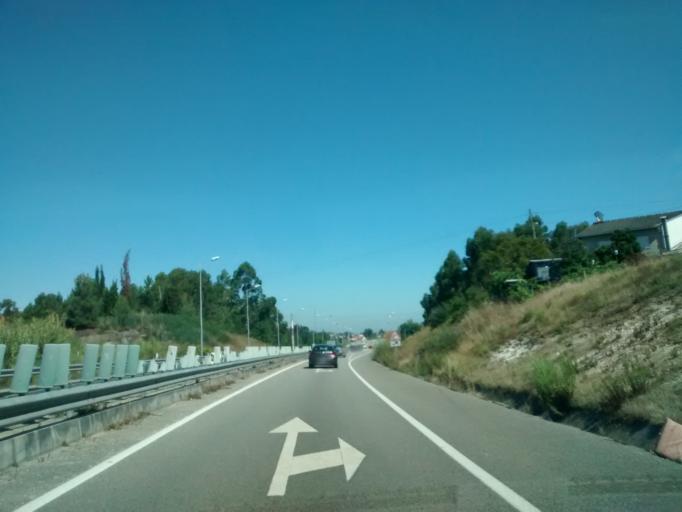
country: PT
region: Aveiro
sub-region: Oliveira do Bairro
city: Oliveira do Bairro
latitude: 40.5193
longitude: -8.5041
